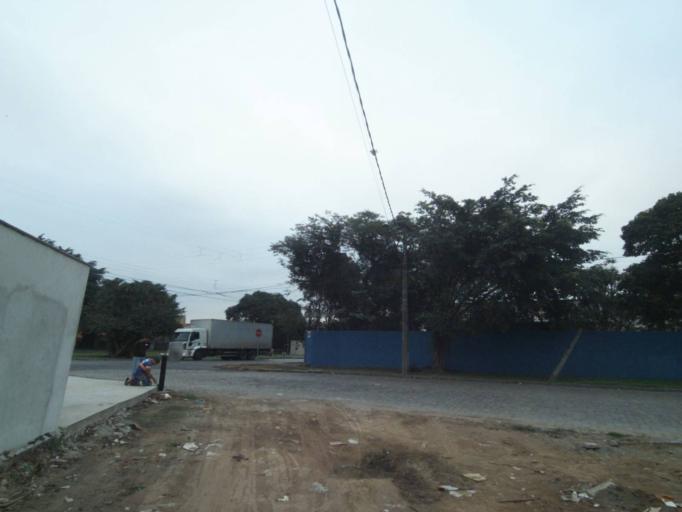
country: BR
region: Parana
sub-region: Paranagua
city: Paranagua
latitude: -25.5144
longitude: -48.5198
